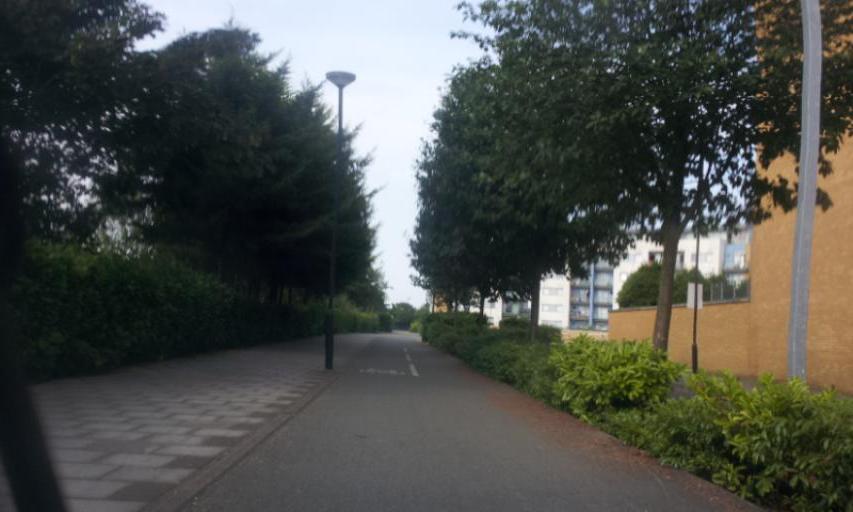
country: GB
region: England
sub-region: Greater London
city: Woolwich
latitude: 51.5011
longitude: 0.0850
